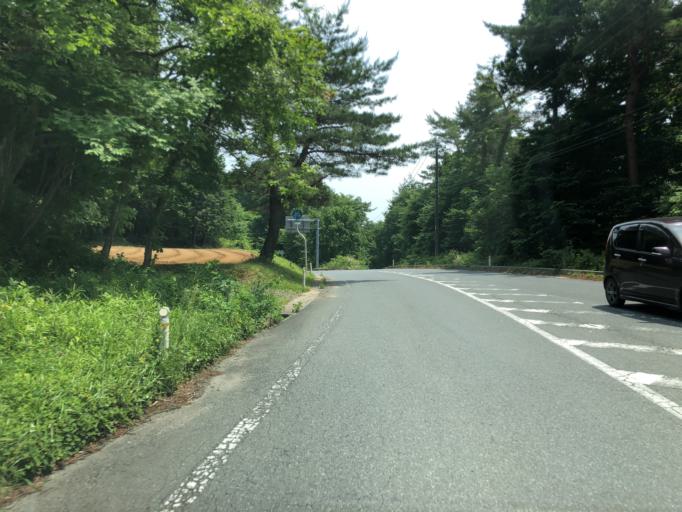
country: JP
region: Fukushima
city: Namie
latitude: 37.5903
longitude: 140.9344
